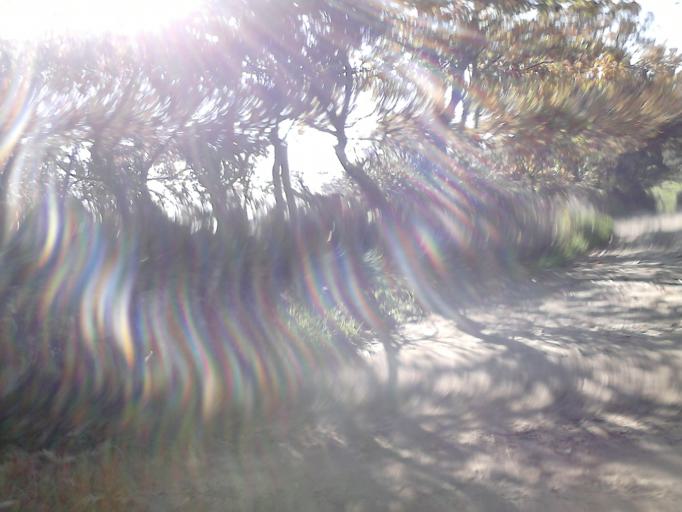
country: ES
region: Madrid
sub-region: Provincia de Madrid
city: El Escorial
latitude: 40.5997
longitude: -4.1030
